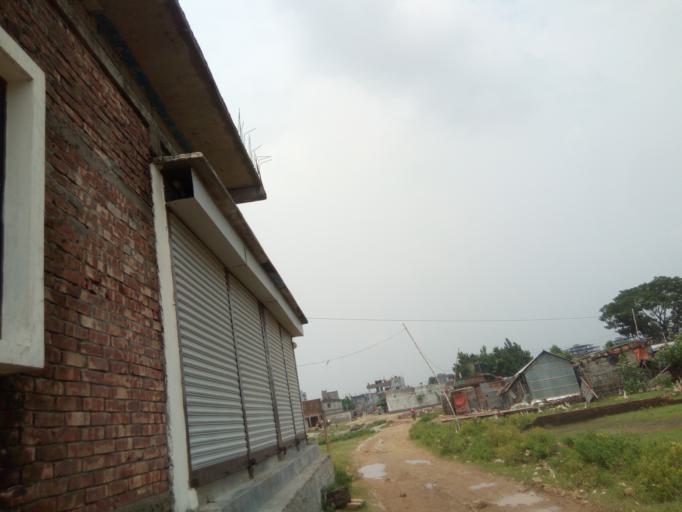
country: BD
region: Dhaka
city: Azimpur
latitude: 23.7421
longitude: 90.3522
